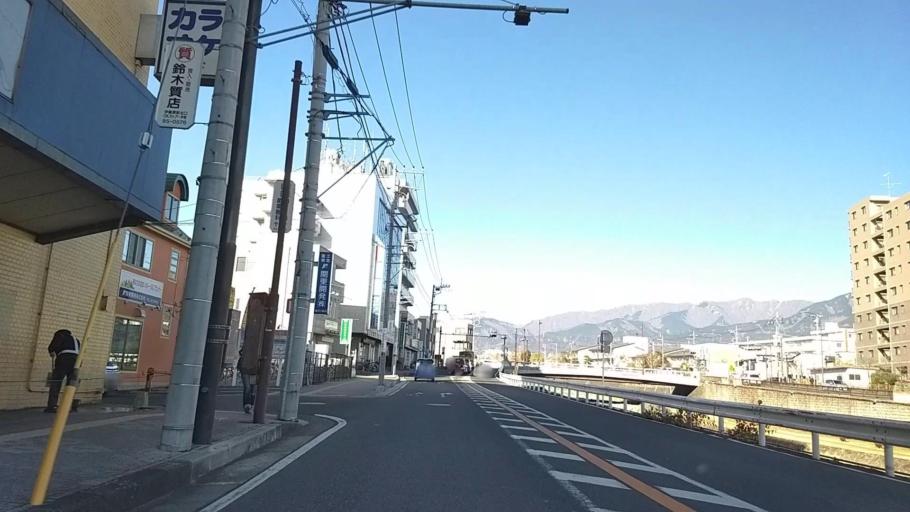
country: JP
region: Kanagawa
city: Hadano
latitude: 35.3716
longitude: 139.2254
